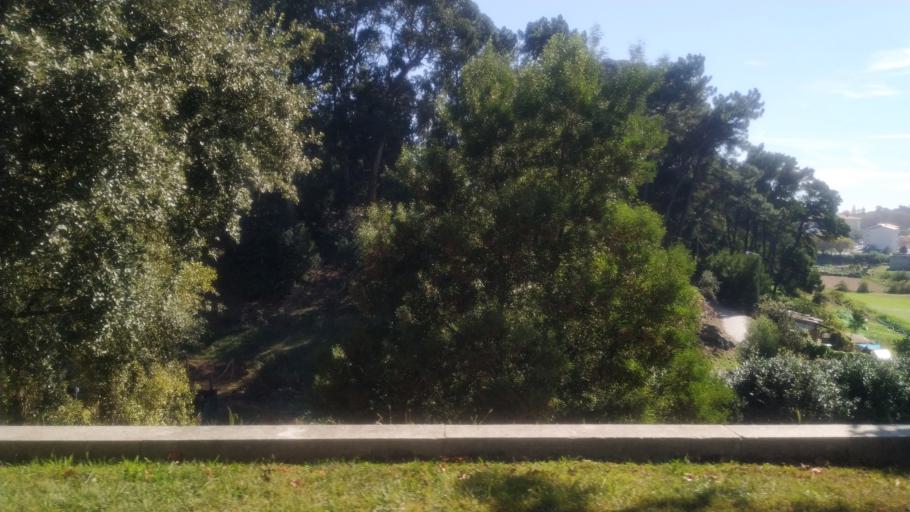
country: PT
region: Porto
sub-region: Matosinhos
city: Matosinhos
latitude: 41.1789
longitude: -8.6728
